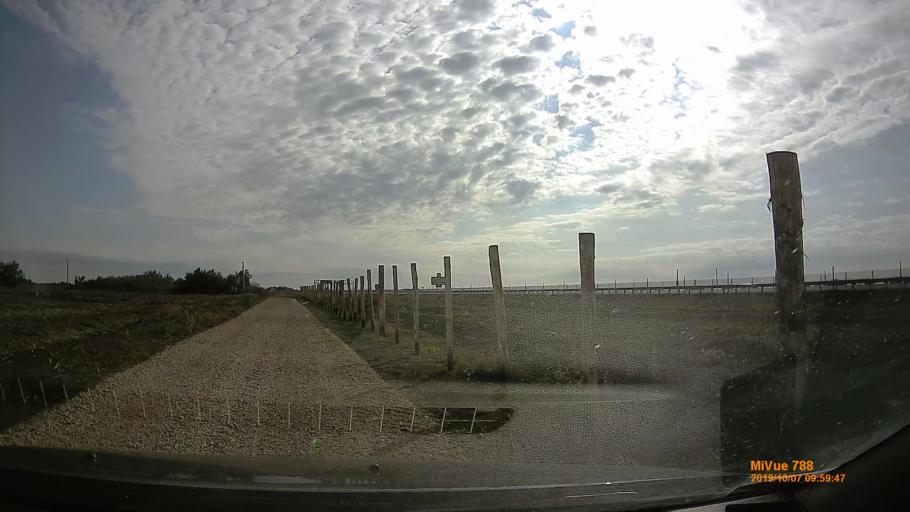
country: HU
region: Bekes
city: Kondoros
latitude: 46.7393
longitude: 20.7885
